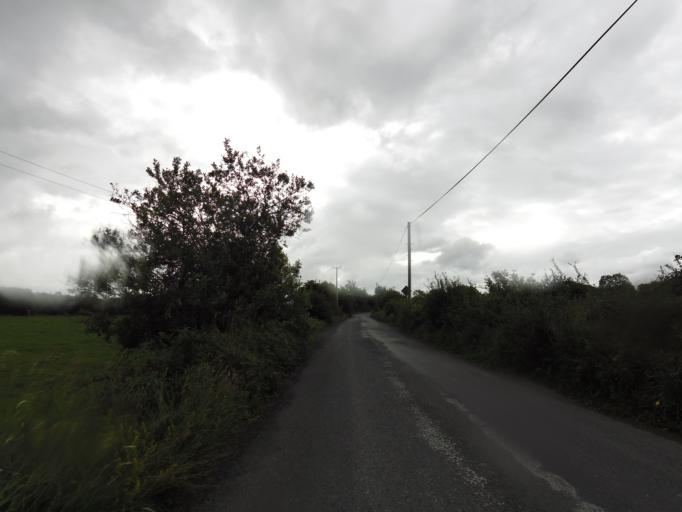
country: IE
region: Connaught
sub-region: County Galway
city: Athenry
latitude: 53.2857
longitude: -8.6900
